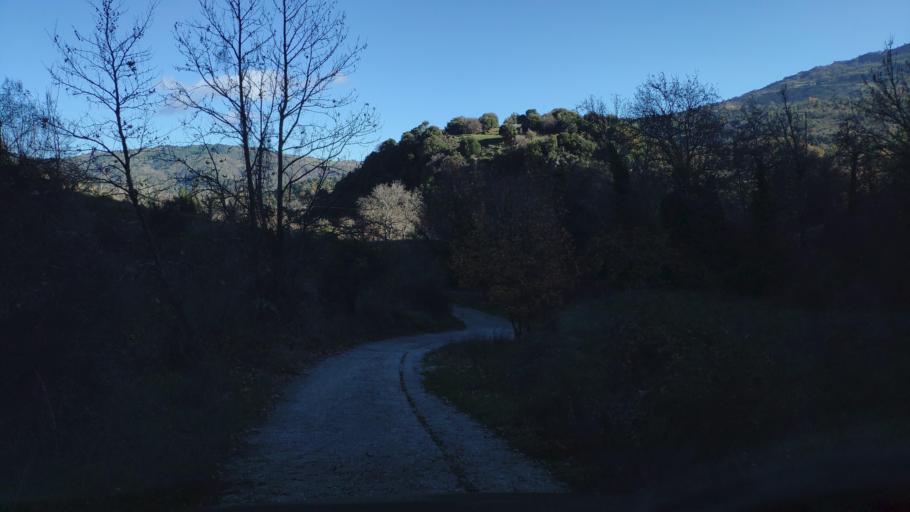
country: GR
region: West Greece
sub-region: Nomos Achaias
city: Aiyira
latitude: 38.0499
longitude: 22.4476
